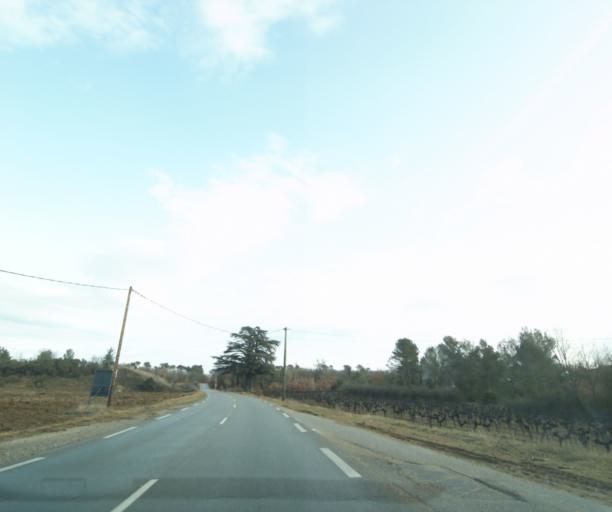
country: FR
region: Provence-Alpes-Cote d'Azur
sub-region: Departement du Var
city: Rougiers
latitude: 43.3997
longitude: 5.8877
